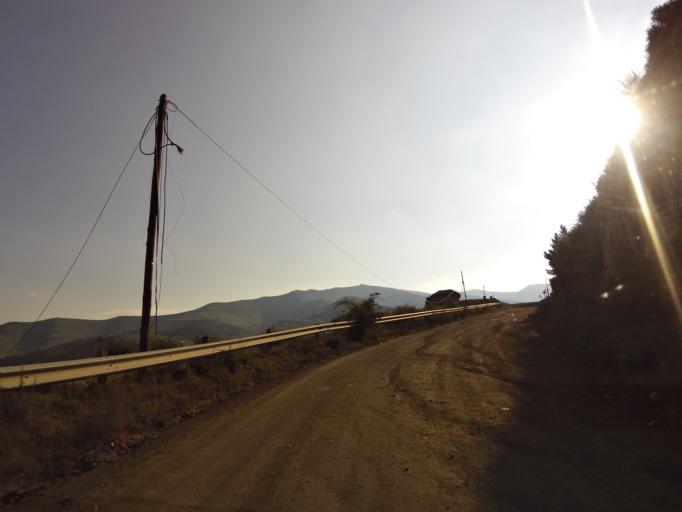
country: LS
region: Butha-Buthe
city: Butha-Buthe
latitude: -29.1055
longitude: 28.4993
